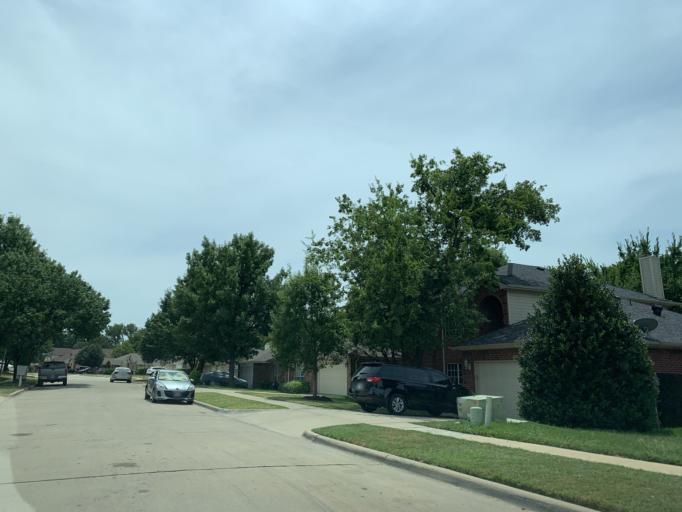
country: US
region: Texas
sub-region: Dallas County
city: Grand Prairie
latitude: 32.6629
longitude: -97.0184
